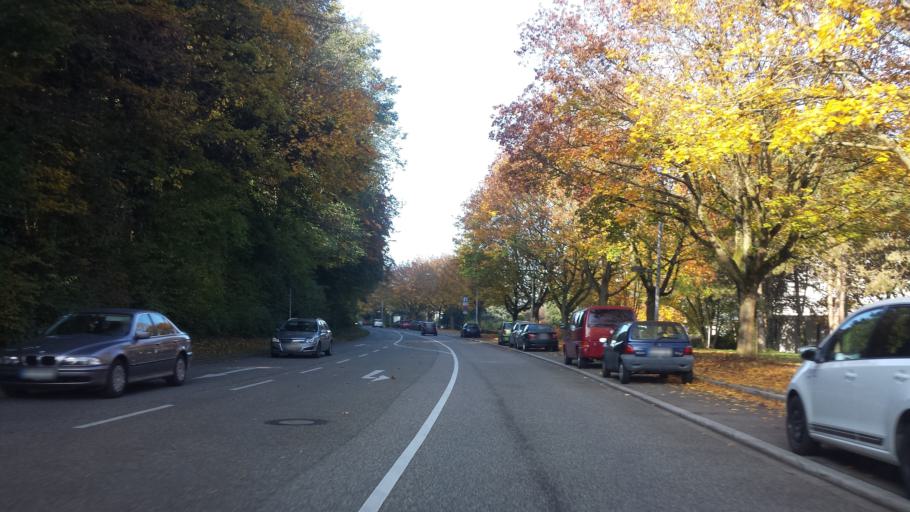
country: DE
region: Baden-Wuerttemberg
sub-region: Karlsruhe Region
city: Bruchsal
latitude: 49.1175
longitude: 8.6167
